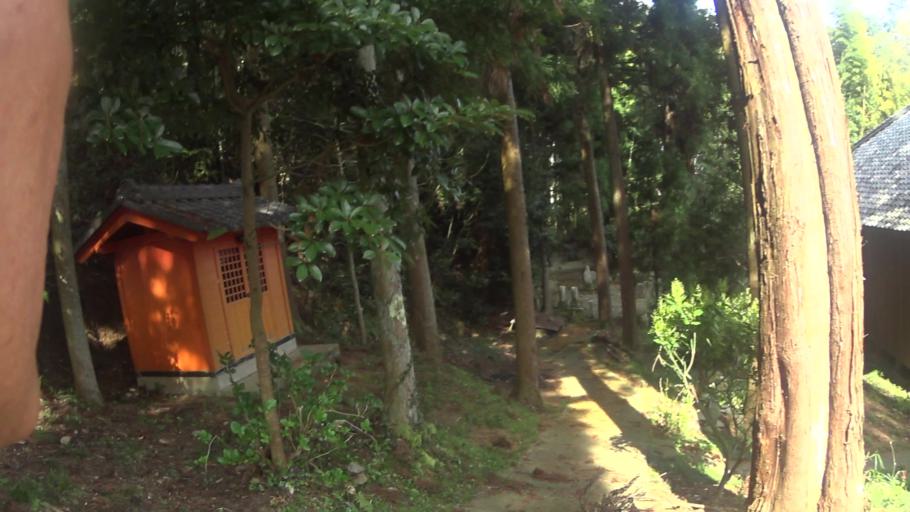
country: JP
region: Kyoto
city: Miyazu
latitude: 35.5841
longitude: 135.1944
